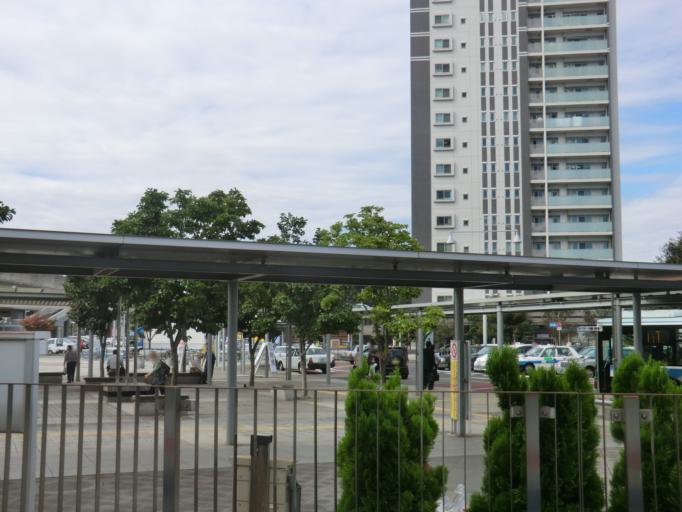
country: JP
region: Ibaraki
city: Moriya
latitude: 35.9509
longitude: 139.9916
